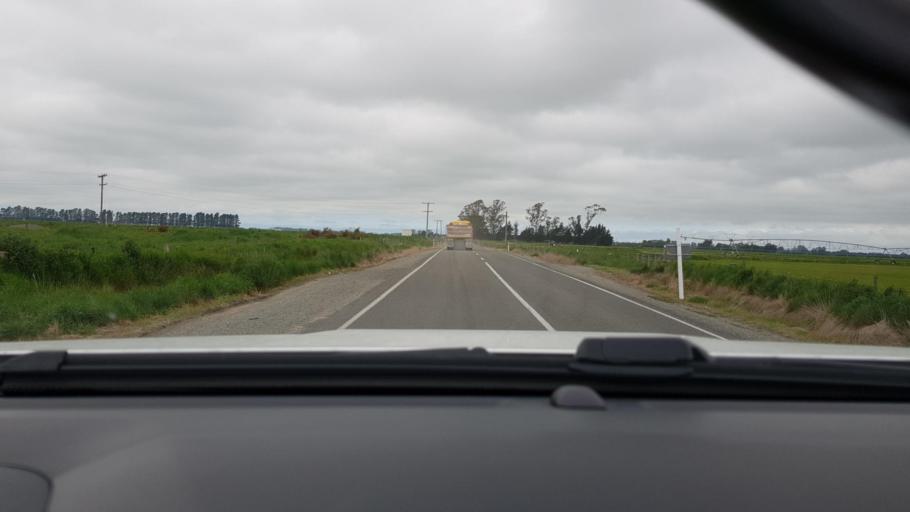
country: NZ
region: Otago
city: Oamaru
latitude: -44.9648
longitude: 170.9573
